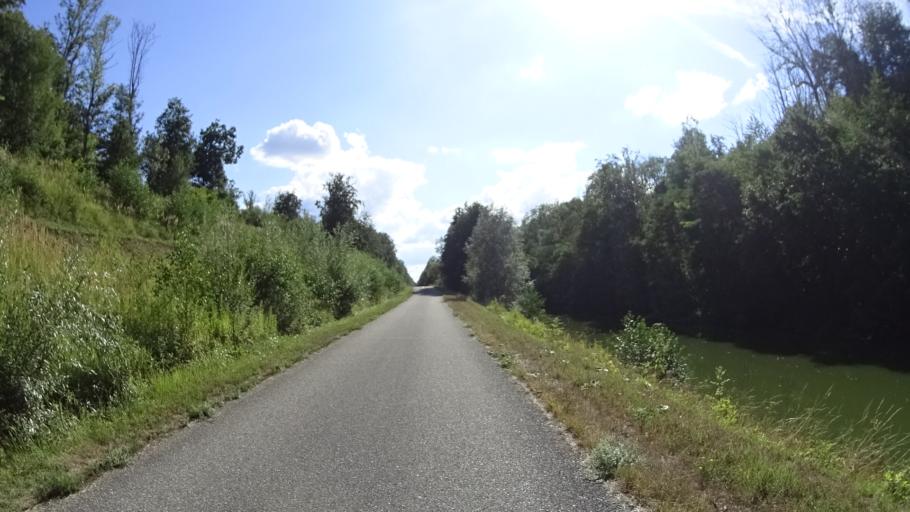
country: FR
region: Franche-Comte
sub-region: Territoire de Belfort
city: Montreux-Chateau
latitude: 47.6281
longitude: 7.0515
